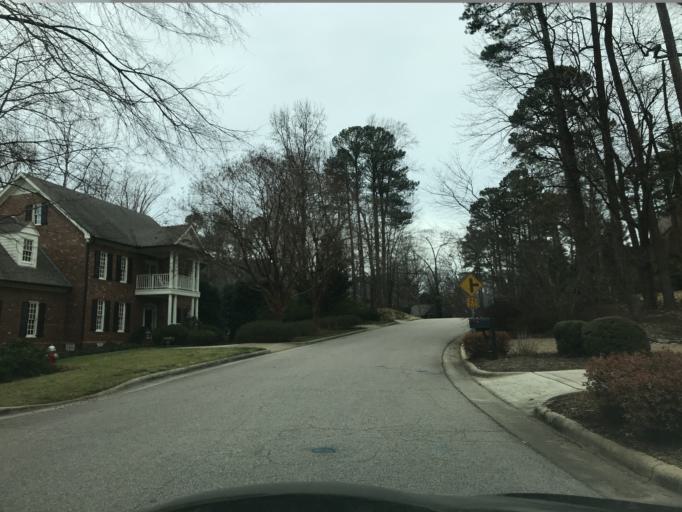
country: US
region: North Carolina
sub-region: Wake County
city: West Raleigh
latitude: 35.8829
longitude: -78.6080
